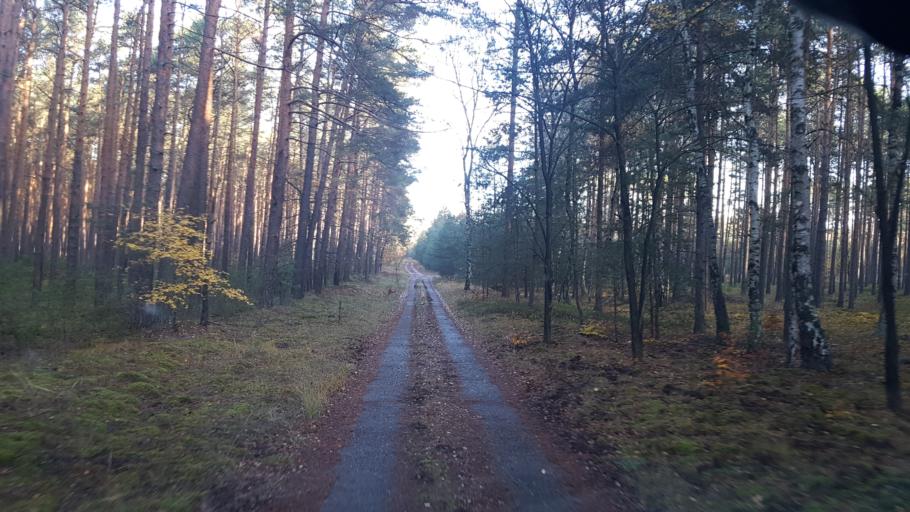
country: DE
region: Brandenburg
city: Crinitz
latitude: 51.7171
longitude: 13.7441
